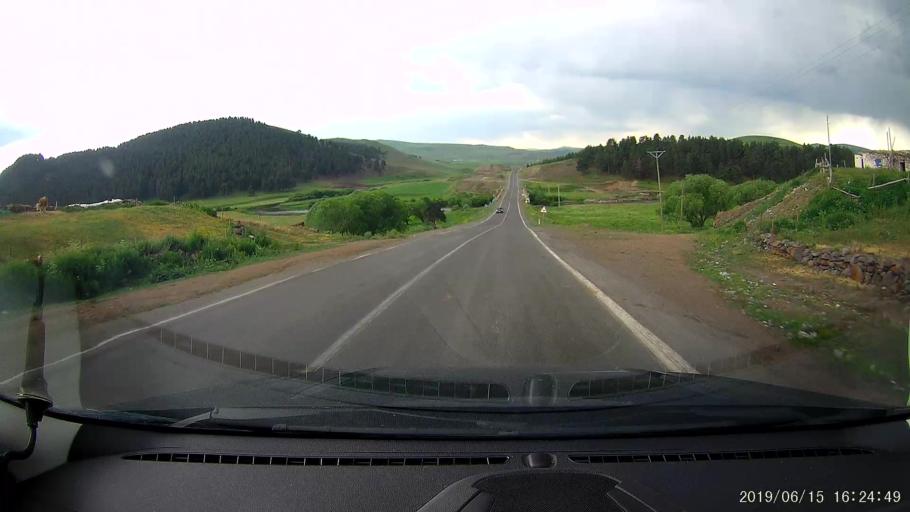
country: TR
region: Ardahan
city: Hanak
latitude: 41.1616
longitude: 42.8724
